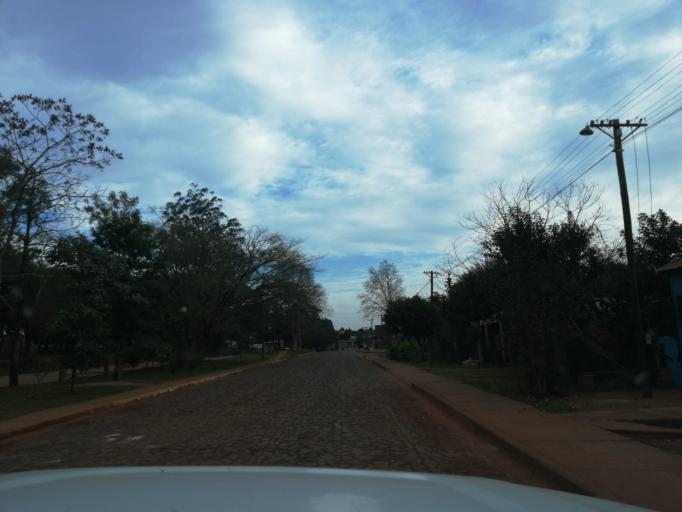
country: AR
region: Misiones
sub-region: Departamento de San Pedro
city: San Pedro
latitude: -26.6250
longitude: -54.0964
